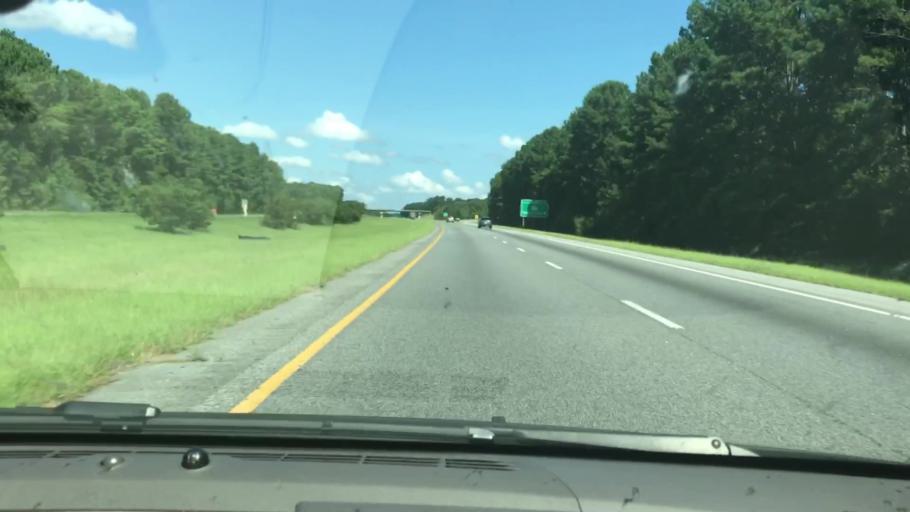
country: US
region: Georgia
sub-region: Harris County
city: Hamilton
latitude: 32.6565
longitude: -84.9756
